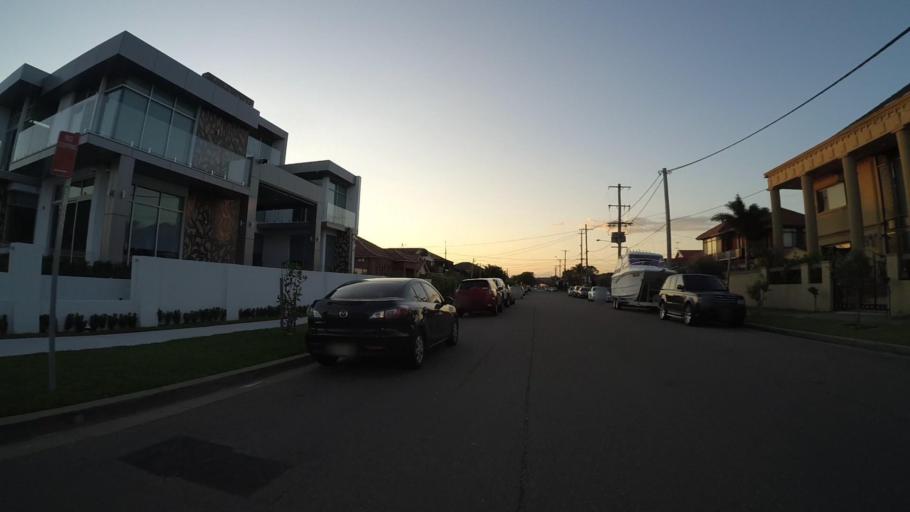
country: AU
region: New South Wales
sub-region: Rockdale
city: Brighton-Le-Sands
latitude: -33.9549
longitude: 151.1600
